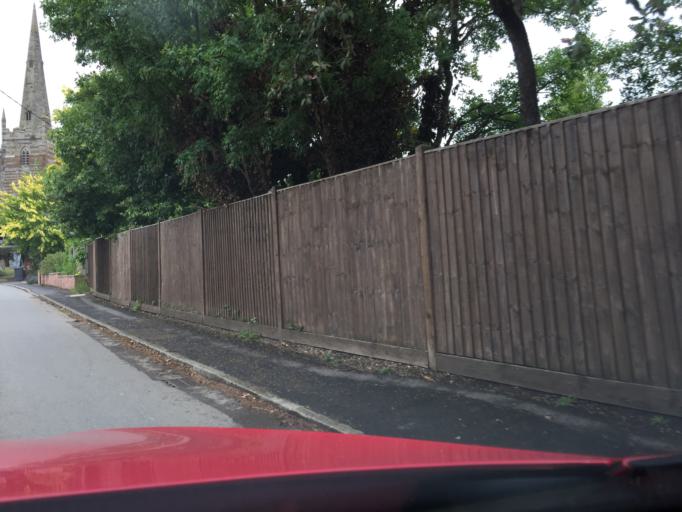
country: GB
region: England
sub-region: Warwickshire
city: Southam
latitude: 52.2260
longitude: -1.3956
